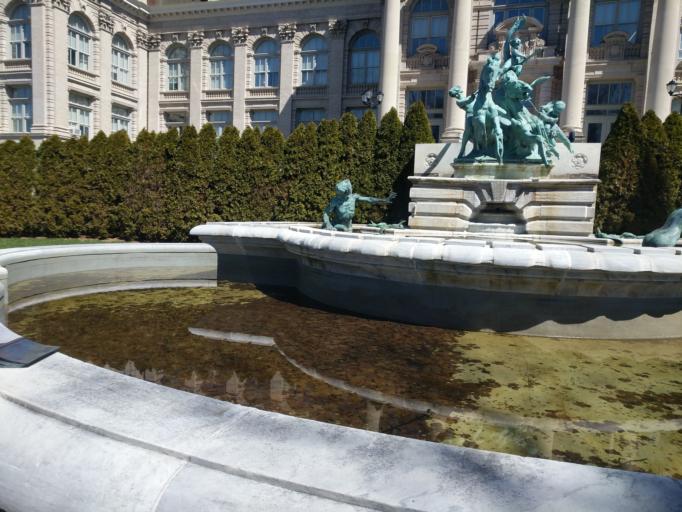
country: US
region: New York
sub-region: Bronx
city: The Bronx
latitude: 40.8665
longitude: -73.8793
